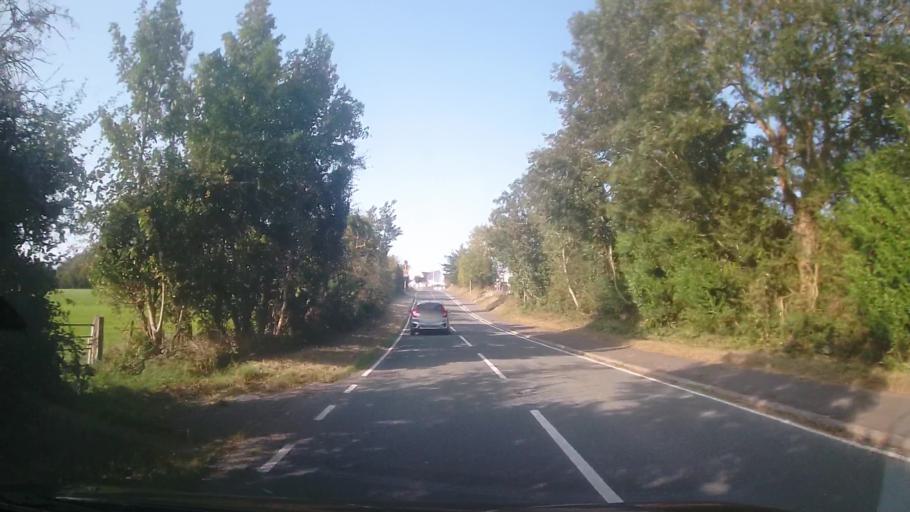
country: GB
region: Wales
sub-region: County of Ceredigion
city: Lledrod
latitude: 52.2865
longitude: -3.8610
